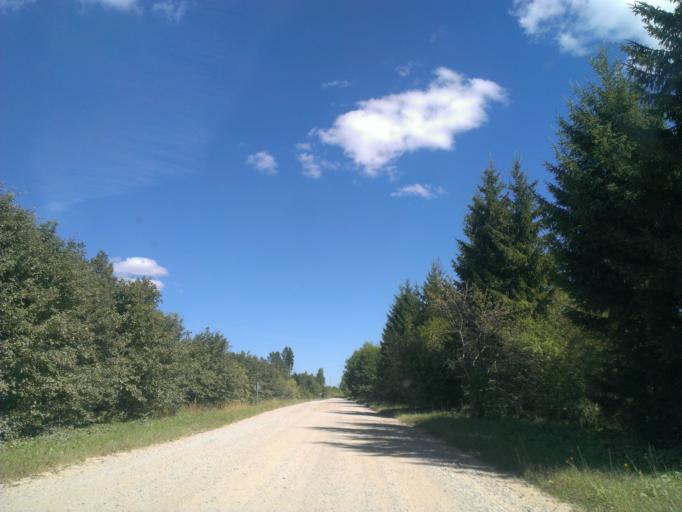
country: LV
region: Malpils
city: Malpils
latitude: 57.0060
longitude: 24.9704
